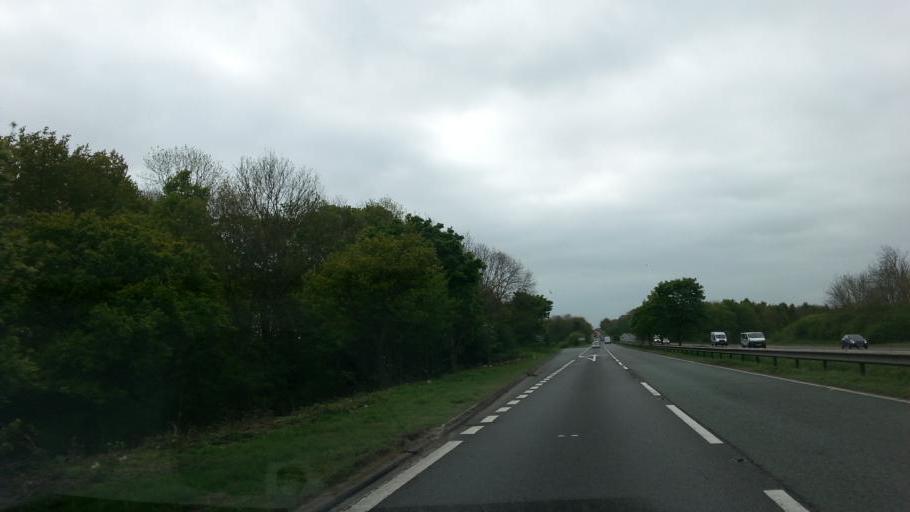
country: GB
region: England
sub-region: District of Rutland
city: Greetham
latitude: 52.7382
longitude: -0.6012
